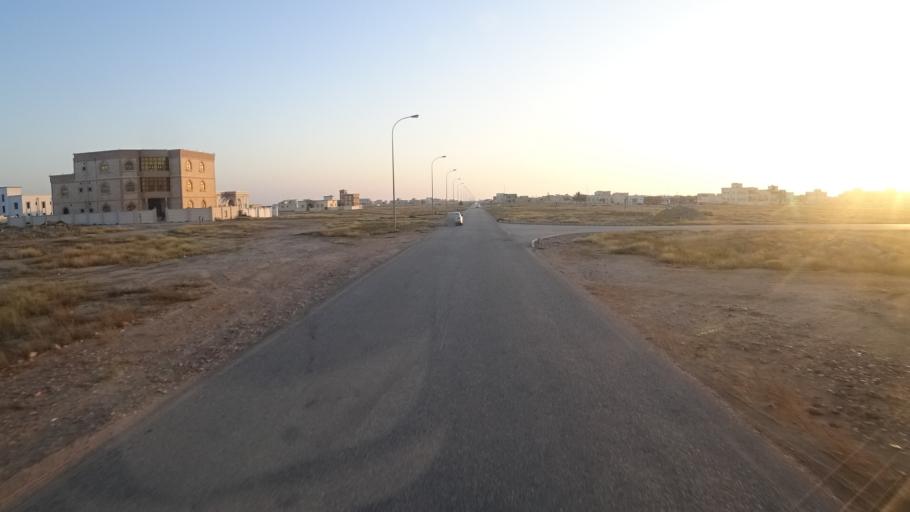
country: OM
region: Zufar
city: Salalah
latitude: 16.9916
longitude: 54.7179
